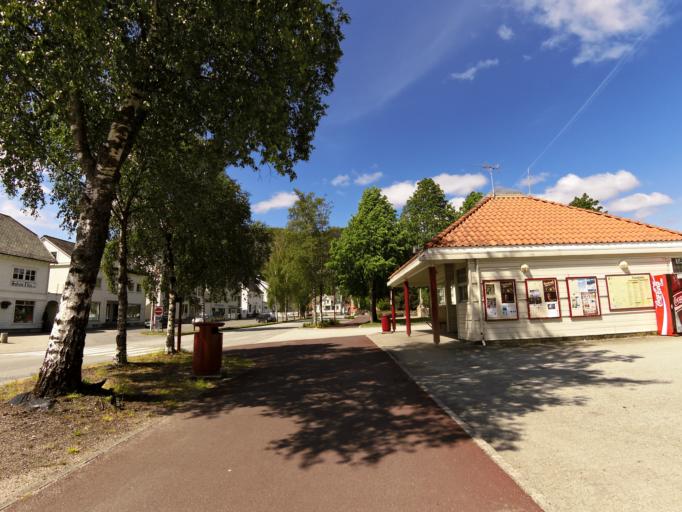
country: NO
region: Vest-Agder
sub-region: Kvinesdal
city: Liknes
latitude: 58.3164
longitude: 6.9624
